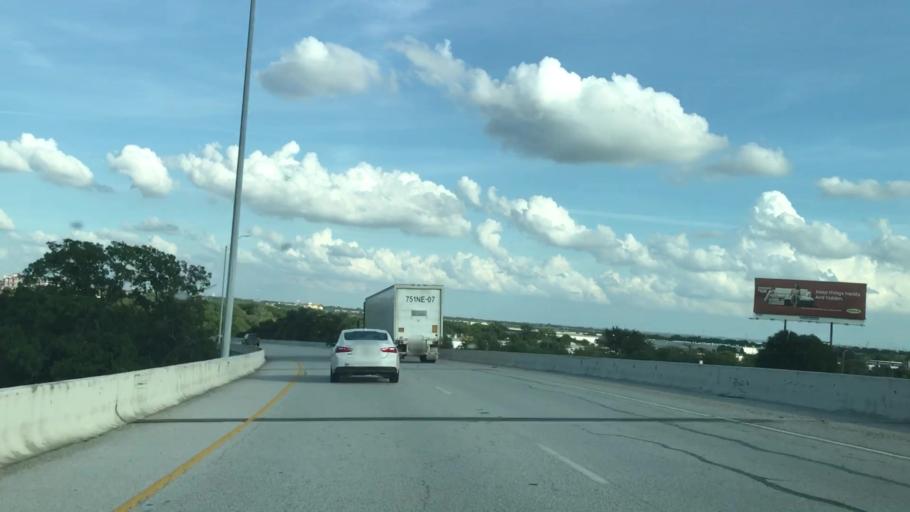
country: US
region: Texas
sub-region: Tarrant County
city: Euless
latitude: 32.8362
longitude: -97.0392
